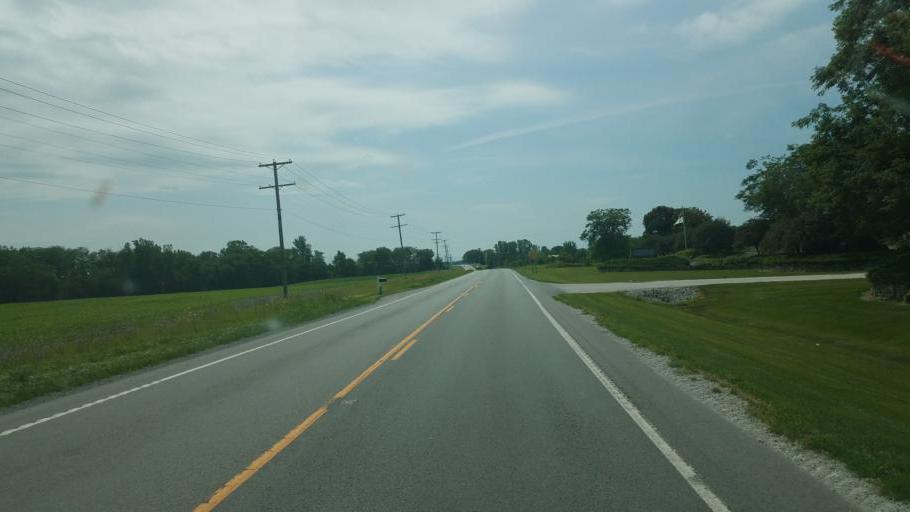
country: US
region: Ohio
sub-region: Wyandot County
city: Upper Sandusky
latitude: 40.8850
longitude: -83.3249
